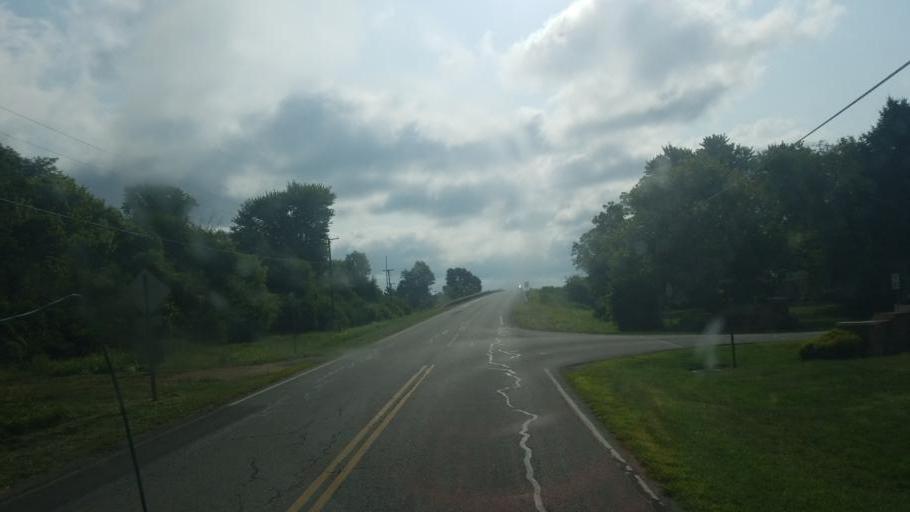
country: US
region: Ohio
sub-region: Marion County
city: Marion
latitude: 40.5691
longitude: -83.0772
